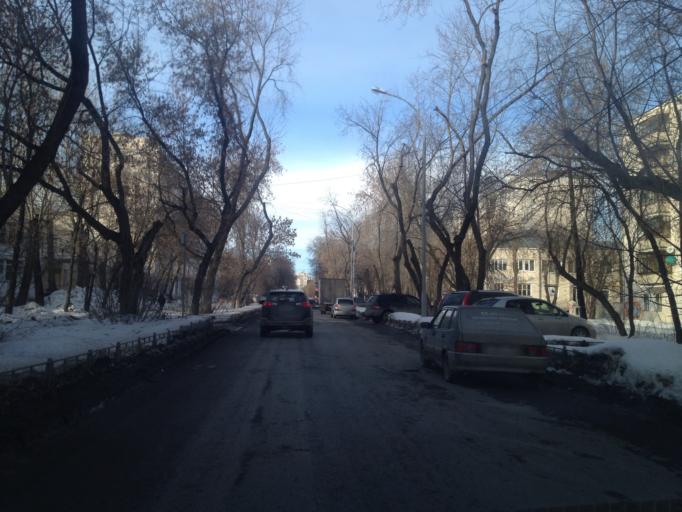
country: RU
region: Sverdlovsk
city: Yekaterinburg
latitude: 56.8390
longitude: 60.6267
